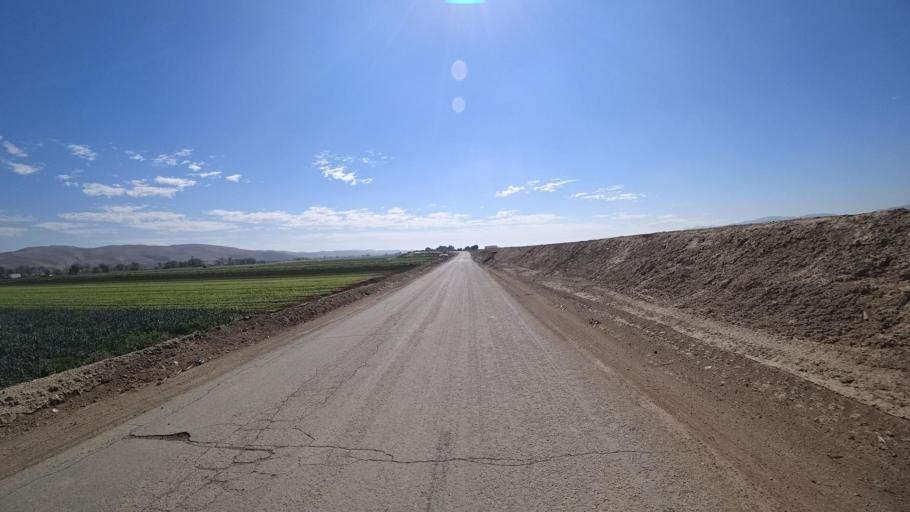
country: US
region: California
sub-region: Monterey County
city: Greenfield
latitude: 36.3310
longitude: -121.2087
